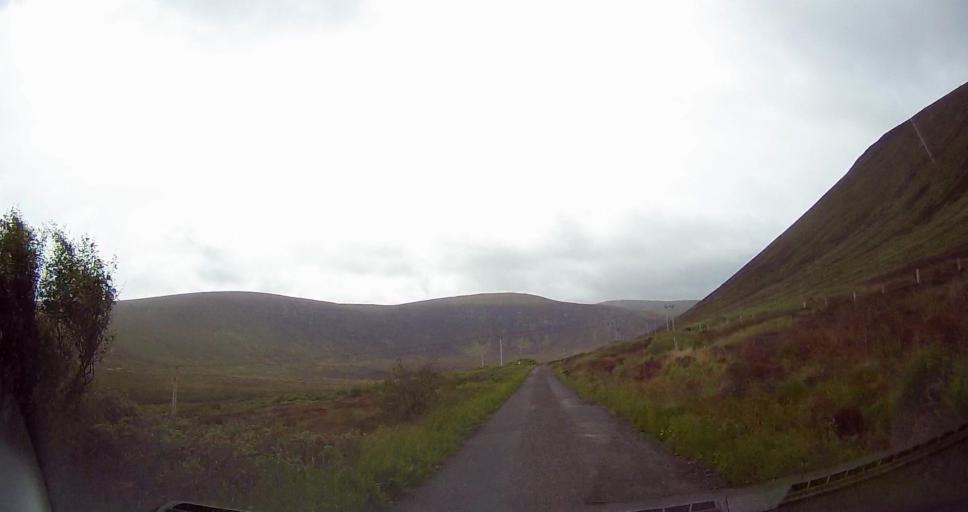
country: GB
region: Scotland
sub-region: Orkney Islands
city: Stromness
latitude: 58.8985
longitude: -3.3145
